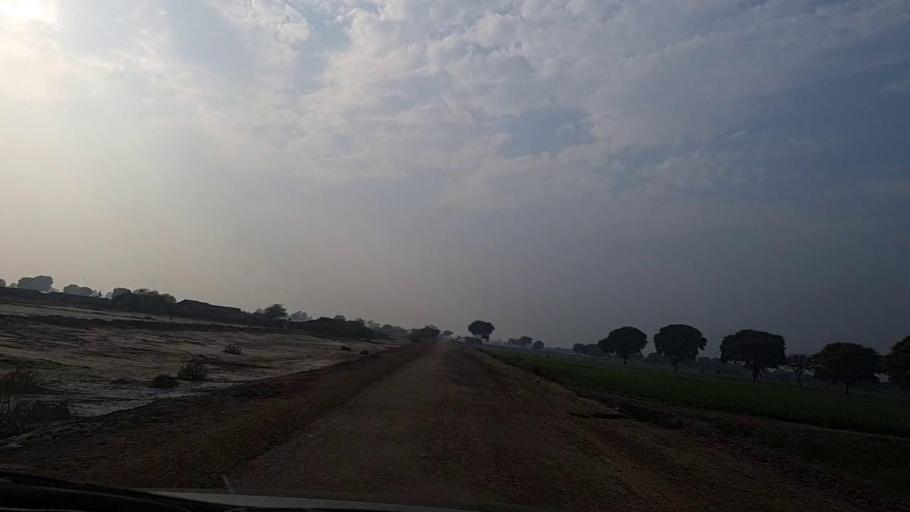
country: PK
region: Sindh
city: Nawabshah
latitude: 26.2738
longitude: 68.3354
